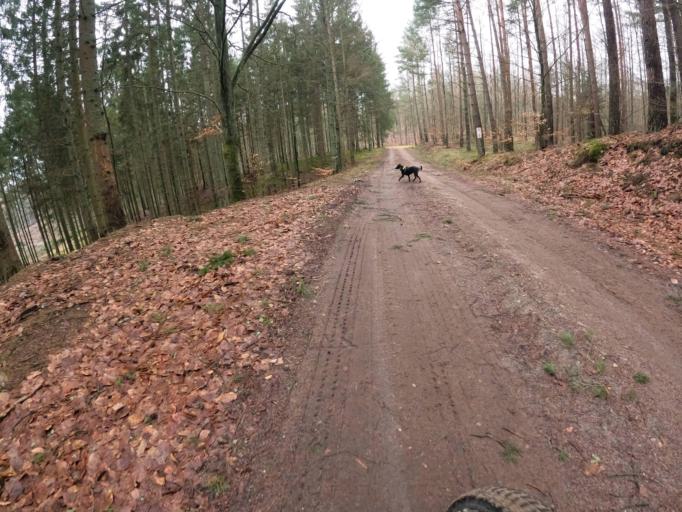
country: PL
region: West Pomeranian Voivodeship
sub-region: Powiat koszalinski
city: Polanow
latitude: 54.2276
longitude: 16.6862
